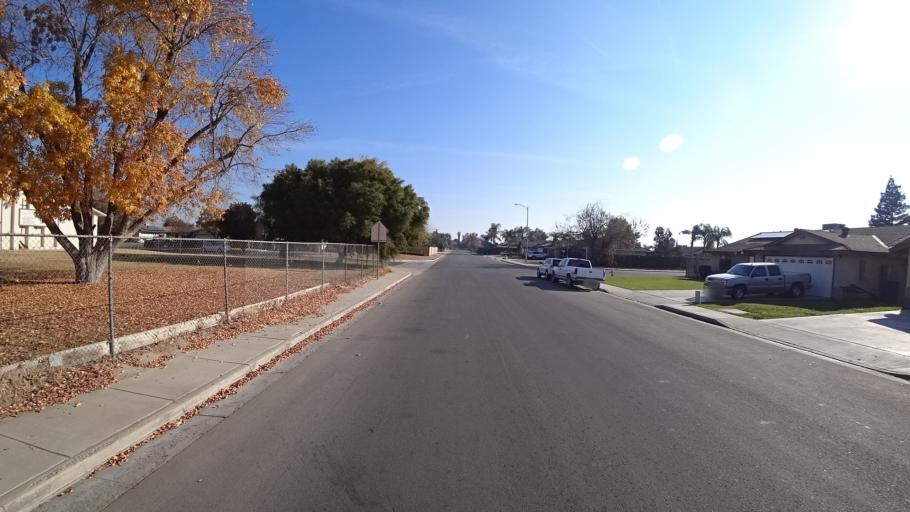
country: US
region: California
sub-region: Kern County
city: Greenfield
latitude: 35.3068
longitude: -119.0247
